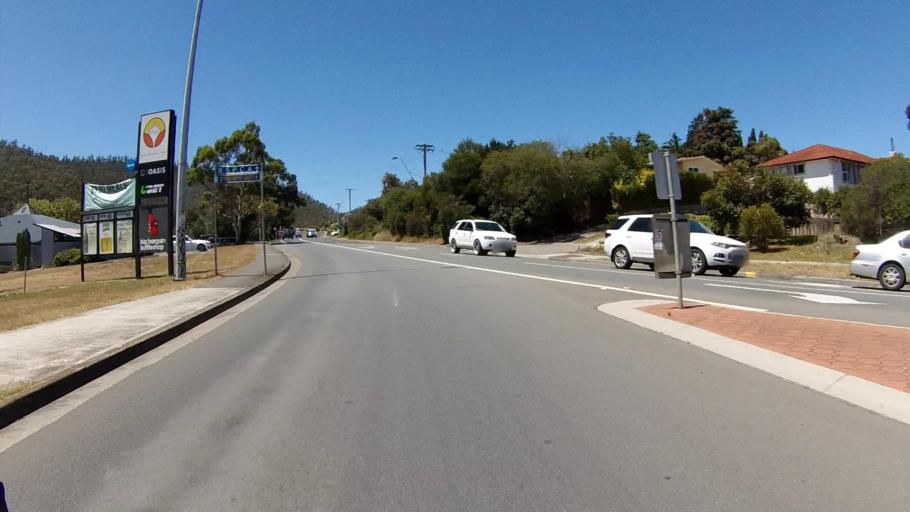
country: AU
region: Tasmania
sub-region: Clarence
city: Warrane
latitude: -42.8561
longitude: 147.3946
